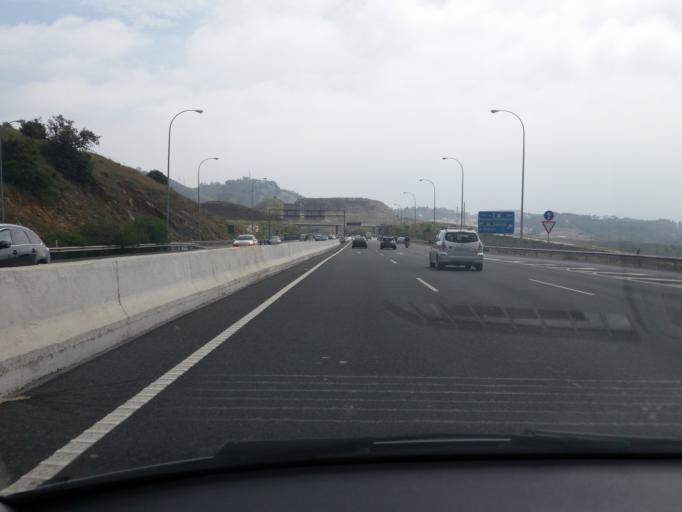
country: ES
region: Andalusia
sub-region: Provincia de Malaga
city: Malaga
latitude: 36.7426
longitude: -4.4044
